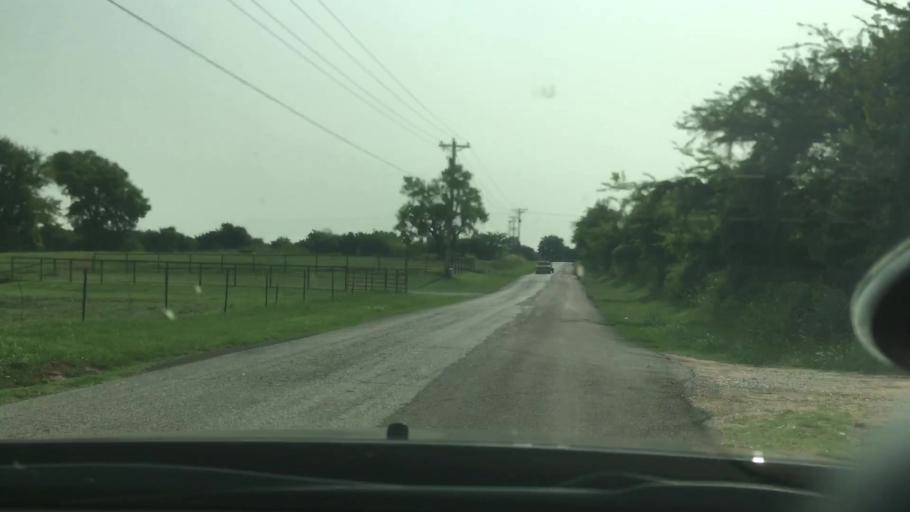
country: US
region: Oklahoma
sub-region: Garvin County
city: Lindsay
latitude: 34.8101
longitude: -97.6115
